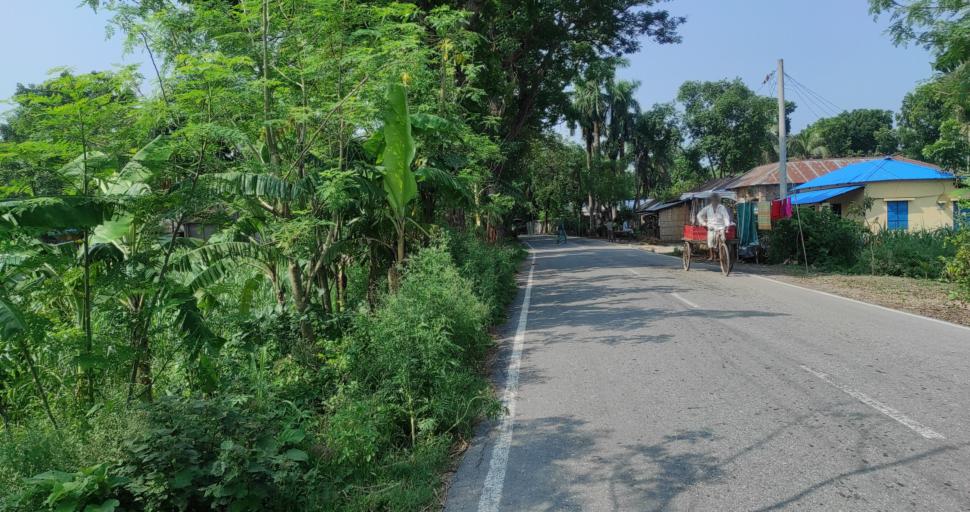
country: BD
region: Rajshahi
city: Ishurdi
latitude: 24.2622
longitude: 89.0495
